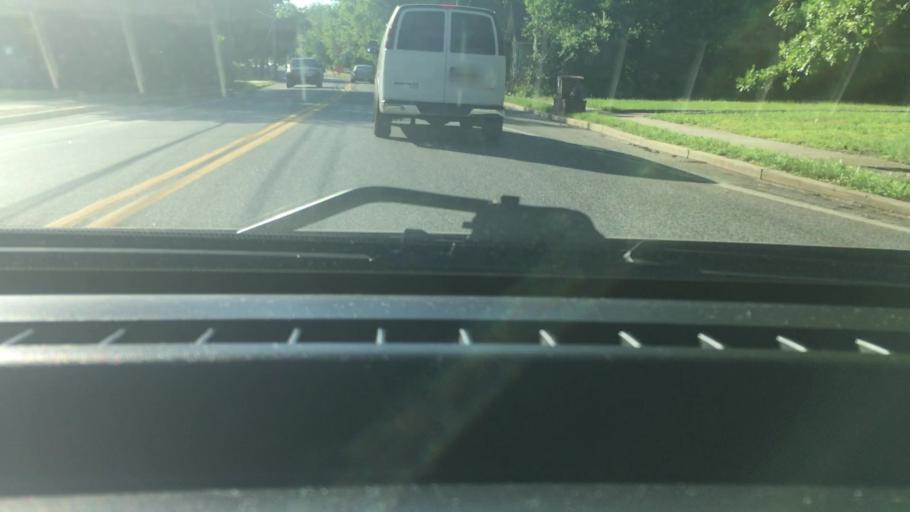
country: US
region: New Jersey
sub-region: Ocean County
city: Island Heights
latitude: 39.9721
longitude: -74.1653
